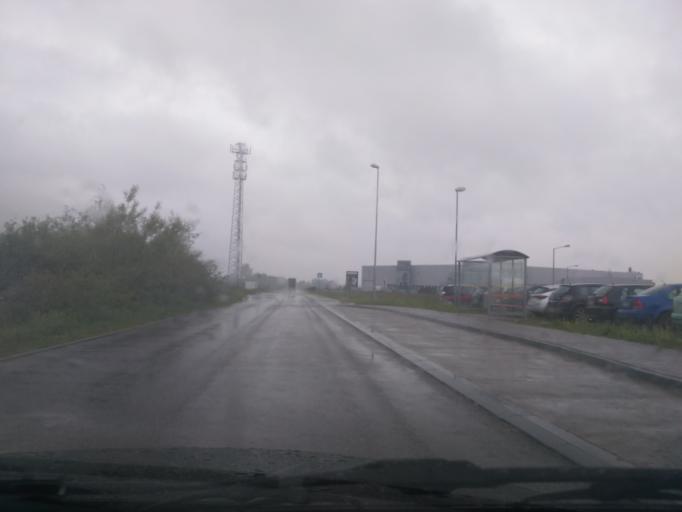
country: PL
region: Subcarpathian Voivodeship
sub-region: Powiat jasielski
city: Tarnowiec
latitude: 49.7501
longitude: 21.5336
